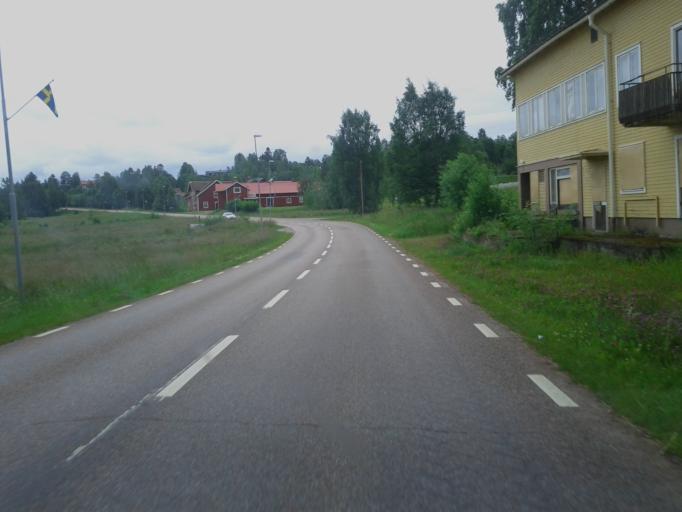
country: NO
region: Hedmark
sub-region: Trysil
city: Innbygda
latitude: 61.6918
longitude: 13.1494
